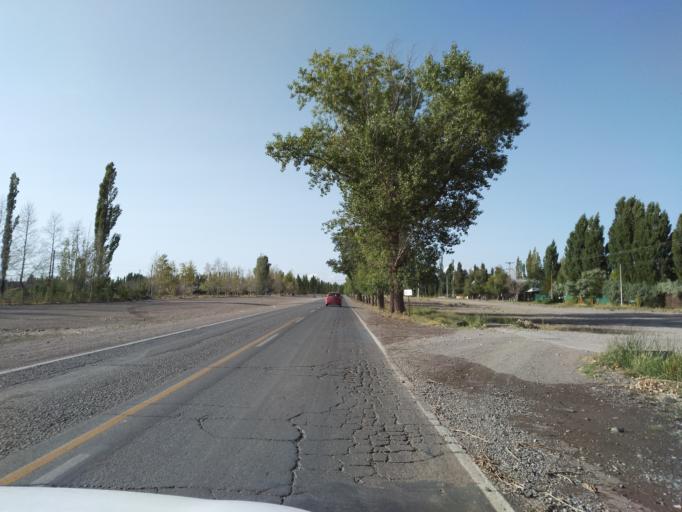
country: AR
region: Mendoza
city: Malargue
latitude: -35.4952
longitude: -69.5857
